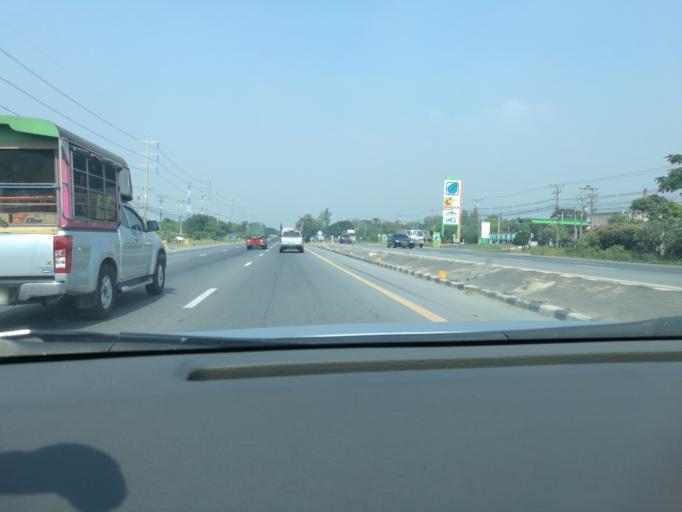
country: TH
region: Sara Buri
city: Chaloem Phra Kiat
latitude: 14.6160
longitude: 100.8924
